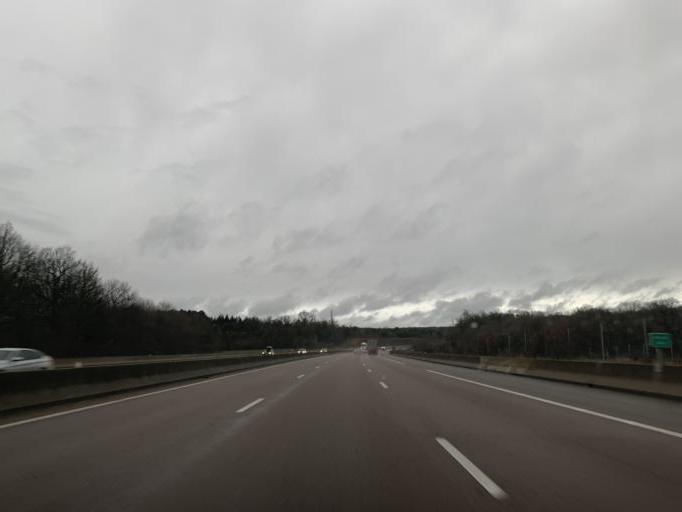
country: FR
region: Bourgogne
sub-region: Departement de la Cote-d'Or
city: Selongey
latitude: 47.7566
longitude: 5.1894
